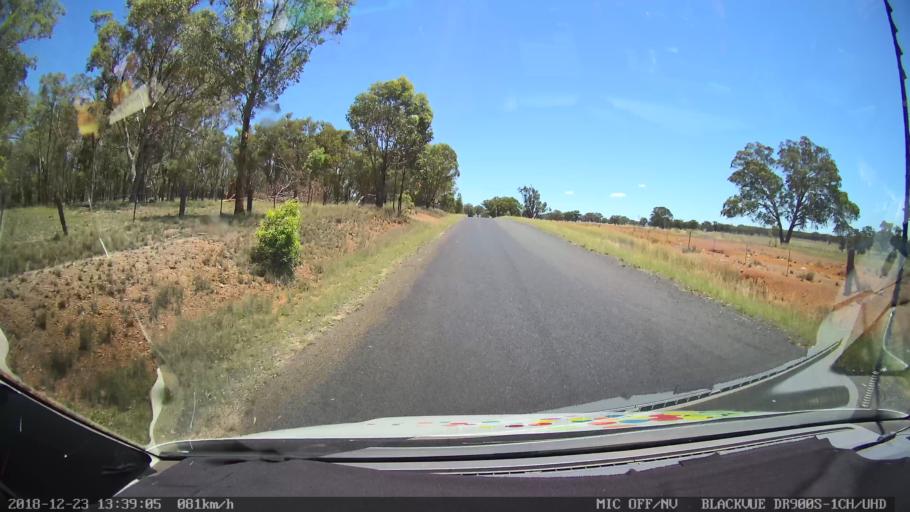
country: AU
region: New South Wales
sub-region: Armidale Dumaresq
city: Armidale
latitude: -30.4552
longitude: 151.2058
